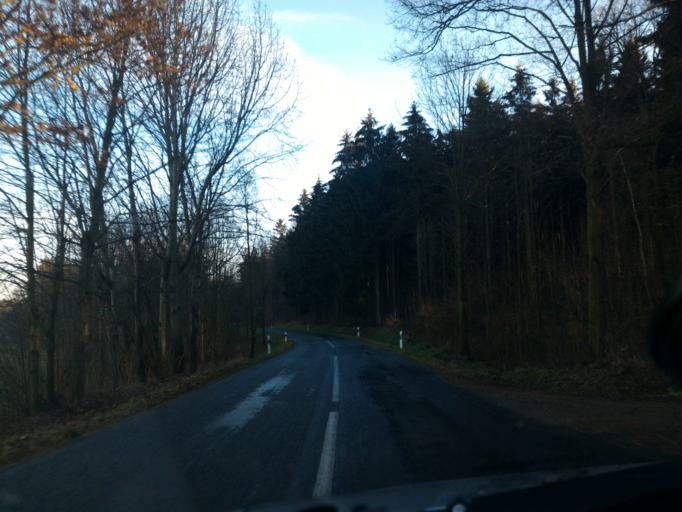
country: DE
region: Saxony
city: Kurort Jonsdorf
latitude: 50.8646
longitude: 14.6738
